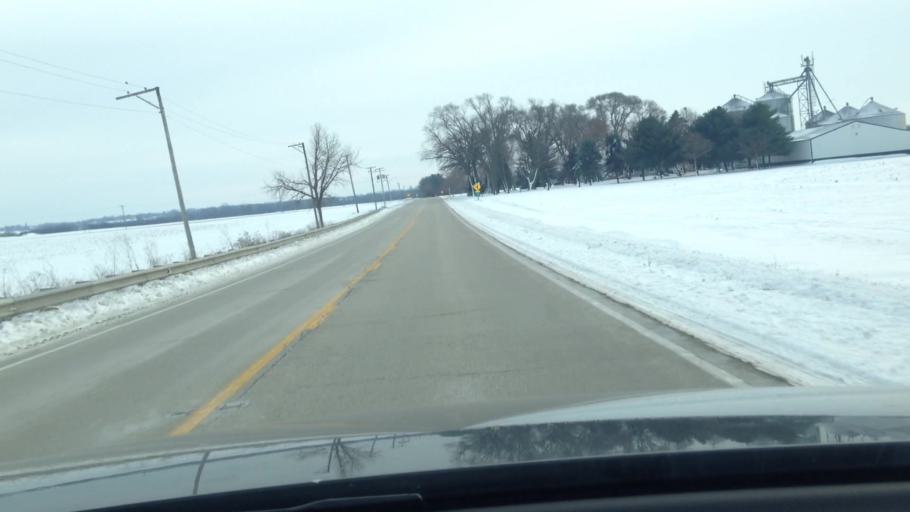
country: US
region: Illinois
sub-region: McHenry County
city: Hebron
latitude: 42.4026
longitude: -88.4382
